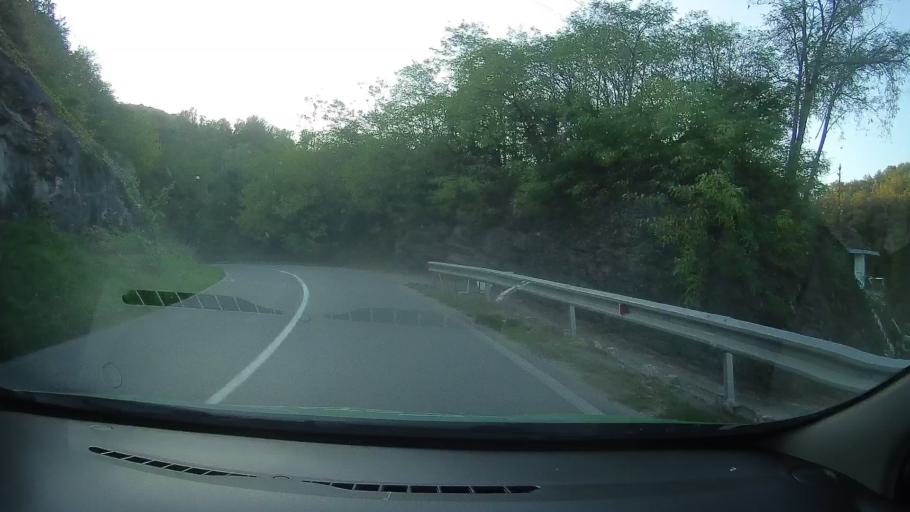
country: RO
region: Timis
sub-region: Comuna Fardea
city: Fardea
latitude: 45.7542
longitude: 22.1249
